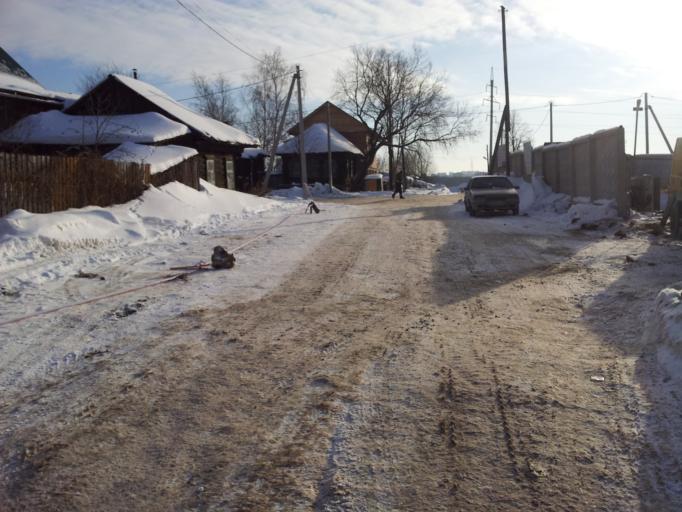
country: RU
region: Perm
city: Perm
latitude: 58.0211
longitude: 56.2634
